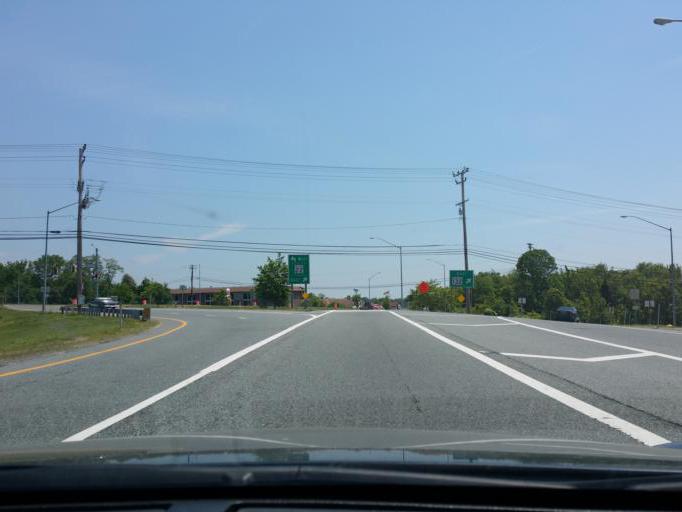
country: US
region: Maryland
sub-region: Harford County
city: Aberdeen
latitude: 39.5246
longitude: -76.1910
